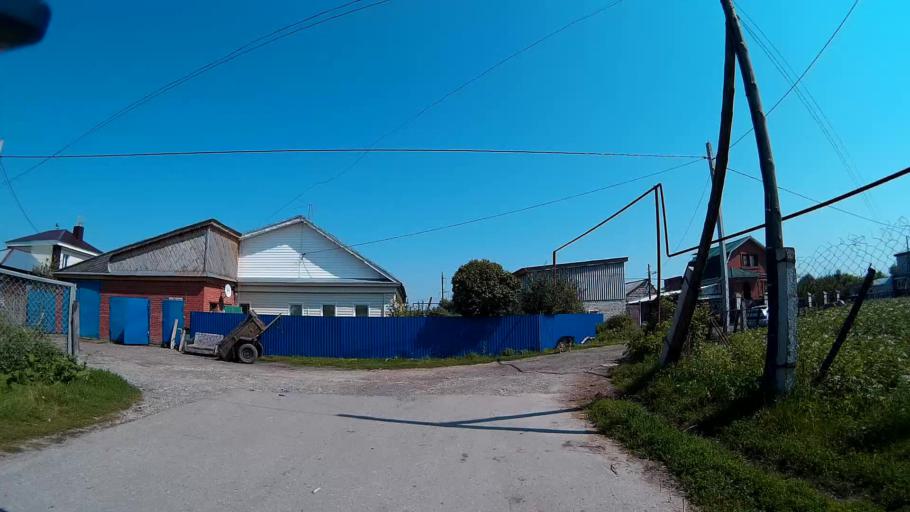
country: RU
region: Ulyanovsk
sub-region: Ulyanovskiy Rayon
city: Ulyanovsk
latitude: 54.2391
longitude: 48.2645
